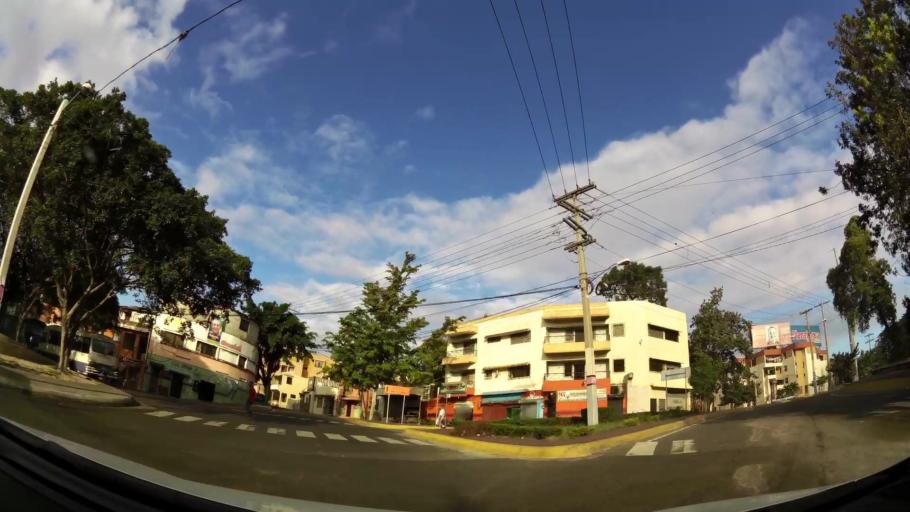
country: DO
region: Nacional
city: San Carlos
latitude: 18.4804
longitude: -69.8849
